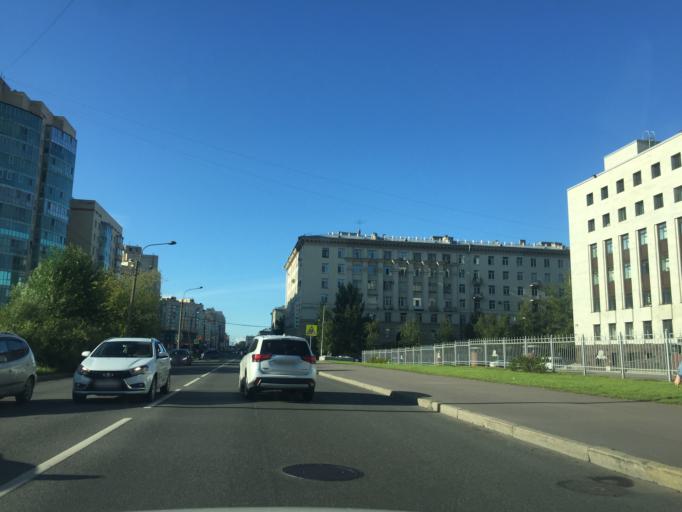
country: RU
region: St.-Petersburg
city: Kupchino
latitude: 59.8652
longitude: 30.3141
